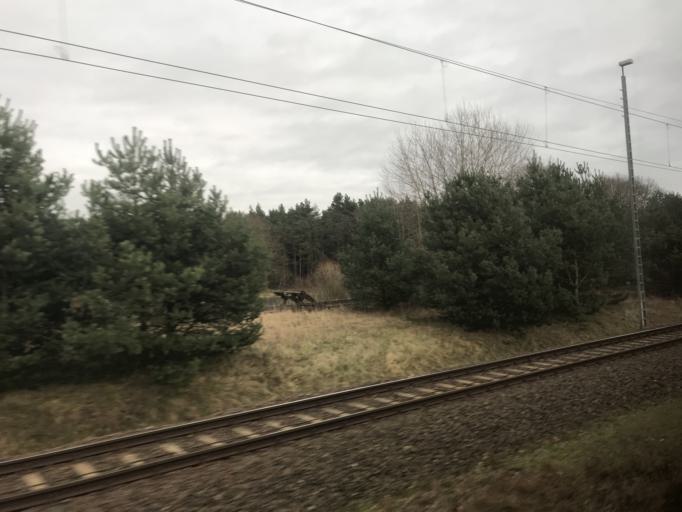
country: DE
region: Lower Saxony
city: Gifhorn
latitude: 52.4534
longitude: 10.5578
